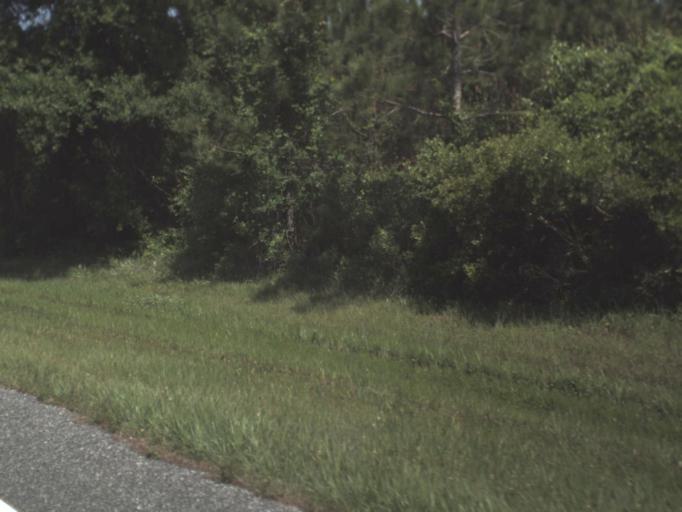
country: US
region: Florida
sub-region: Clay County
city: Middleburg
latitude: 29.9784
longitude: -81.9255
